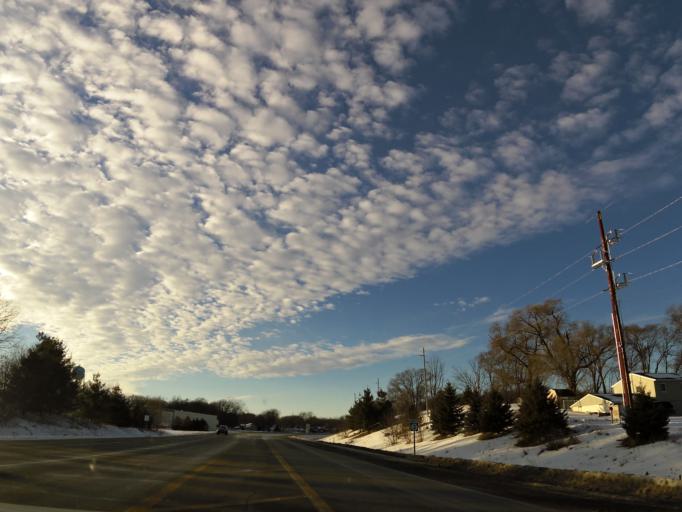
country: US
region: Iowa
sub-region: Butler County
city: Shell Rock
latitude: 42.7159
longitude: -92.5748
